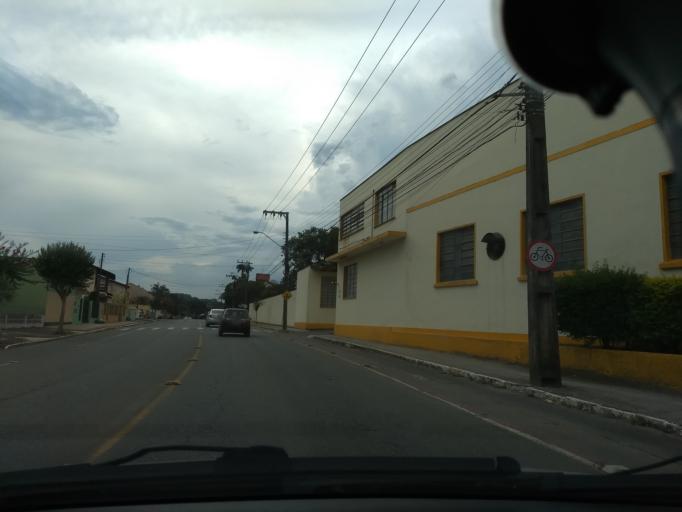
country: BR
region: Santa Catarina
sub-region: Jaragua Do Sul
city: Jaragua do Sul
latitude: -26.4728
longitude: -49.1032
